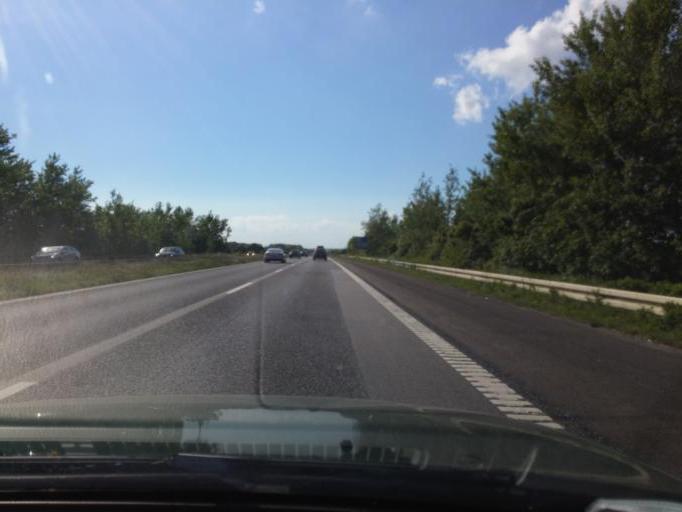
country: DK
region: South Denmark
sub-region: Assens Kommune
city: Arup
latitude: 55.4199
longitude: 10.0218
